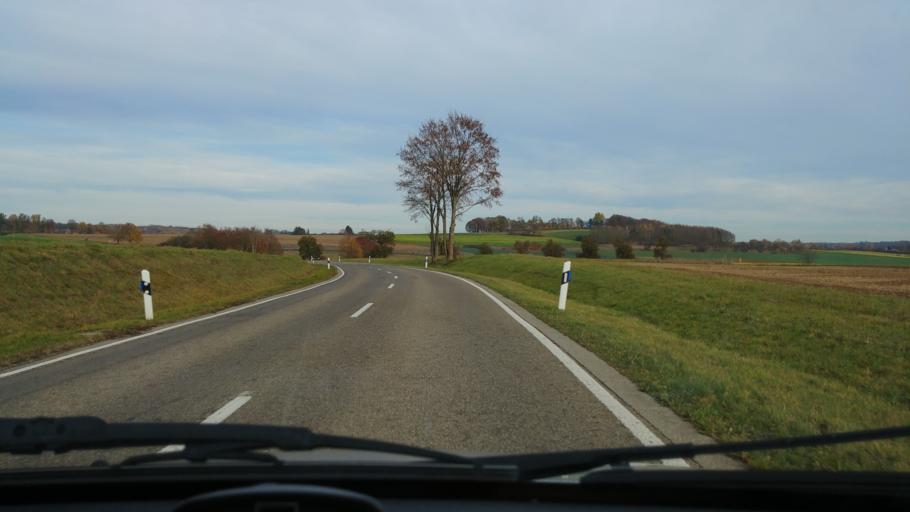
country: DE
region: Bavaria
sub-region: Swabia
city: Ziertheim
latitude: 48.6623
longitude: 10.3605
